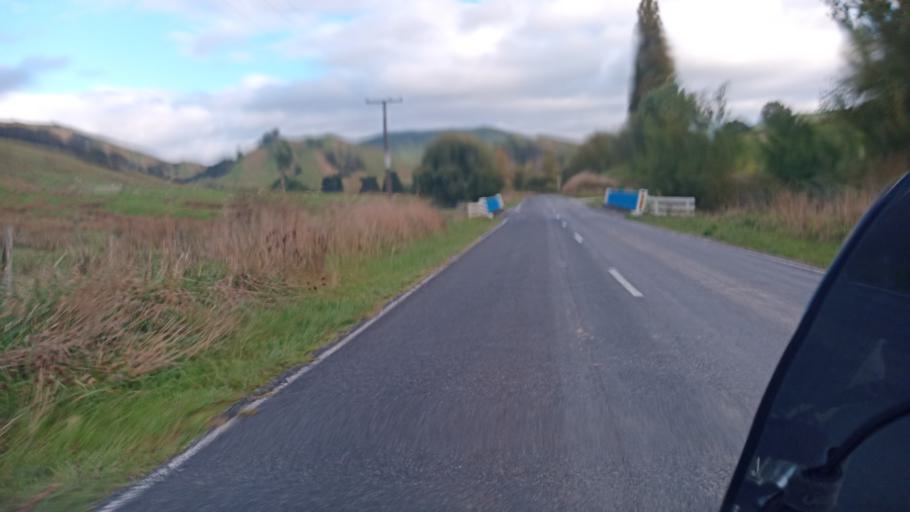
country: NZ
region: Gisborne
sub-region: Gisborne District
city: Gisborne
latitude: -38.5821
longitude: 177.7471
